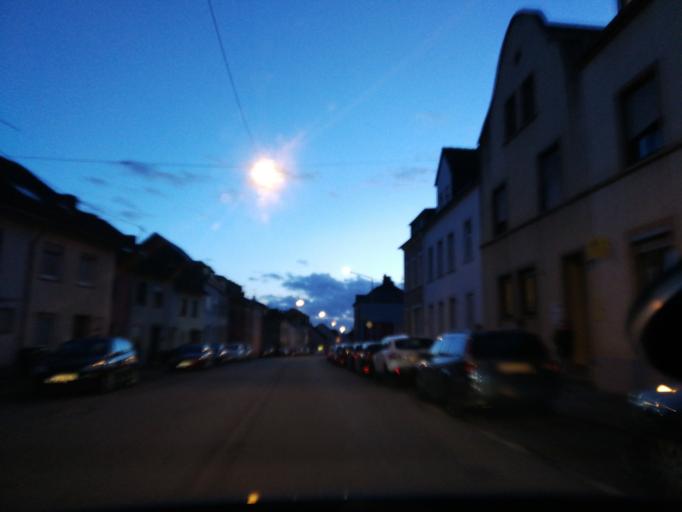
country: DE
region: Rheinland-Pfalz
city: Trier
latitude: 49.7820
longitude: 6.6693
